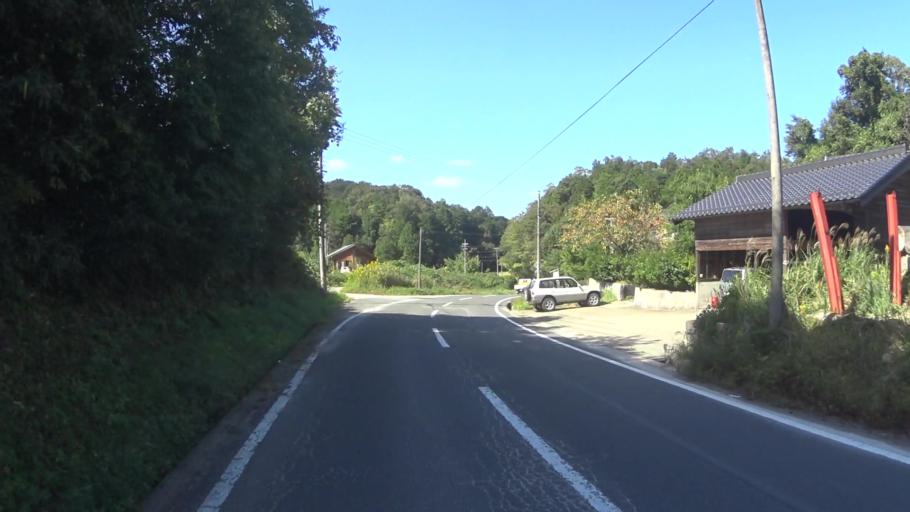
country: JP
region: Hyogo
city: Toyooka
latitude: 35.5928
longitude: 134.9524
